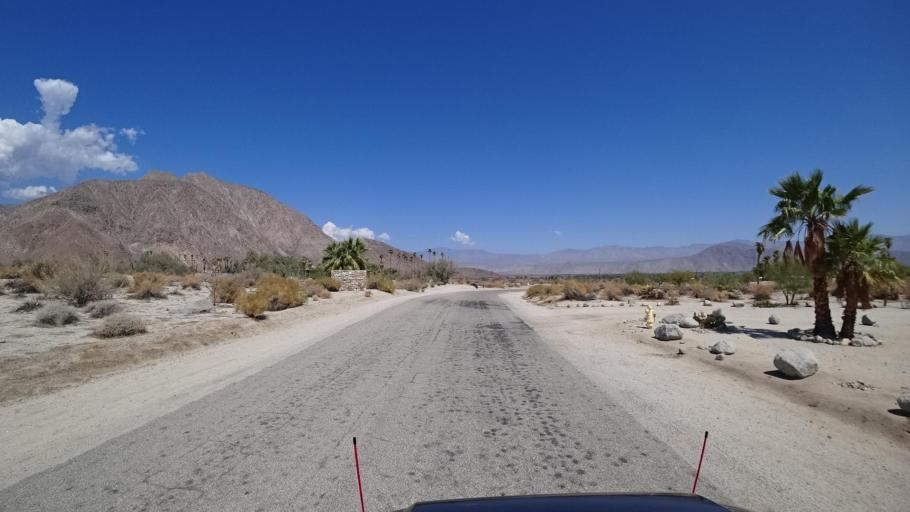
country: US
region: California
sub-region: San Diego County
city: Borrego Springs
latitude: 33.2671
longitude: -116.3996
